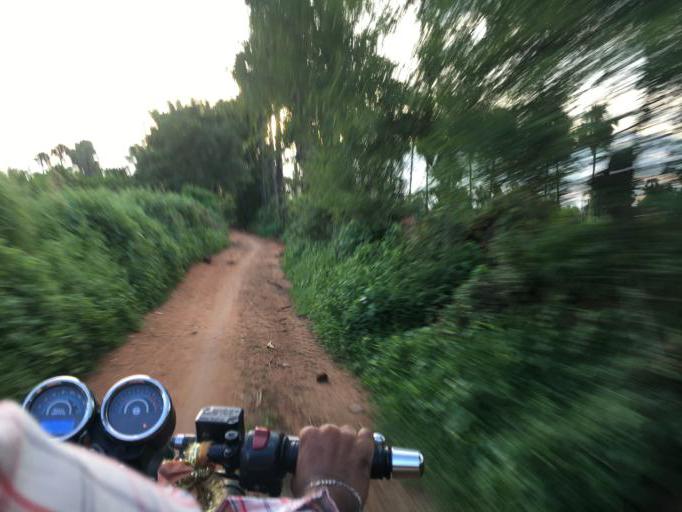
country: IN
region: Telangana
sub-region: Nalgonda
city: Nalgonda
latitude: 17.1763
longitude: 79.4142
